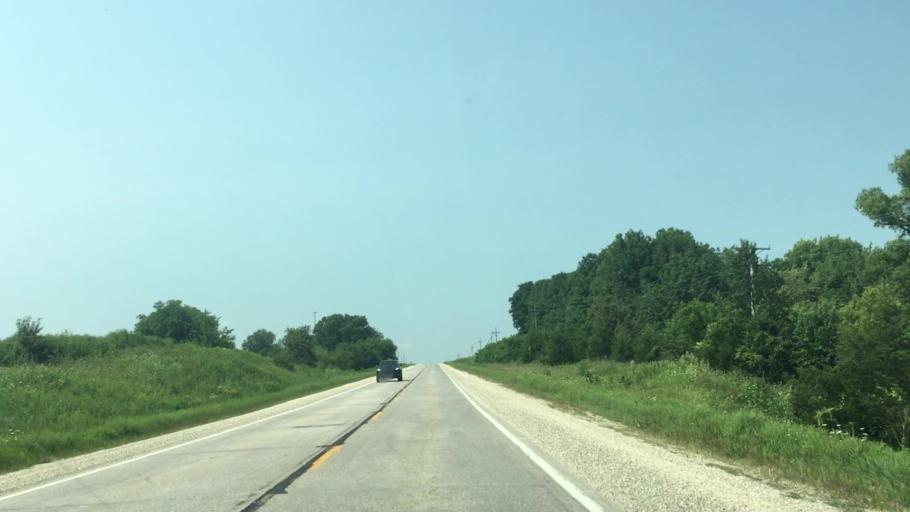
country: US
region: Iowa
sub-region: Fayette County
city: West Union
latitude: 43.0852
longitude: -91.8479
